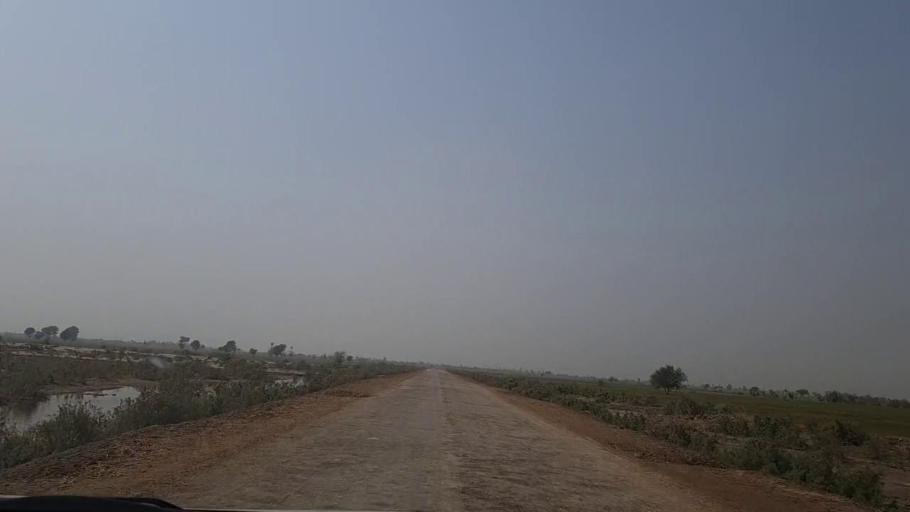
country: PK
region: Sindh
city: Pithoro
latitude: 25.5484
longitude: 69.2240
